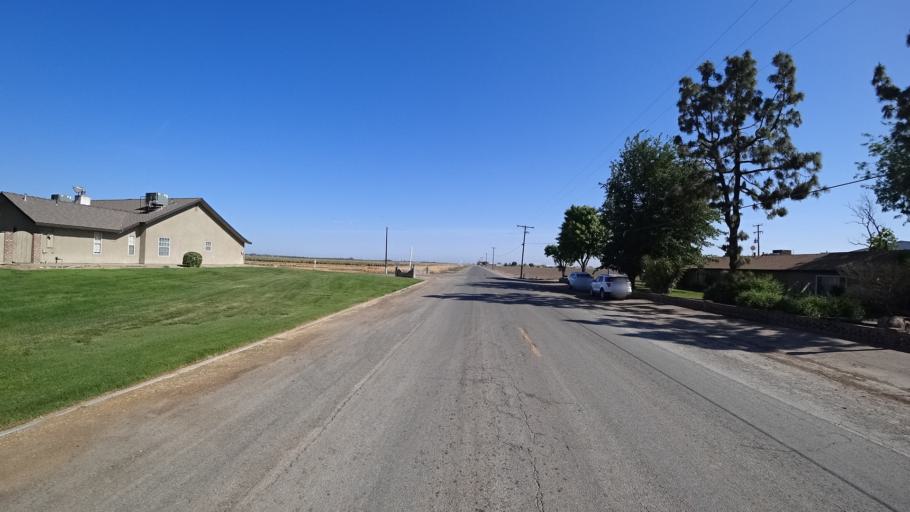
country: US
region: California
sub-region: Kings County
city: Home Garden
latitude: 36.2473
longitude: -119.5473
